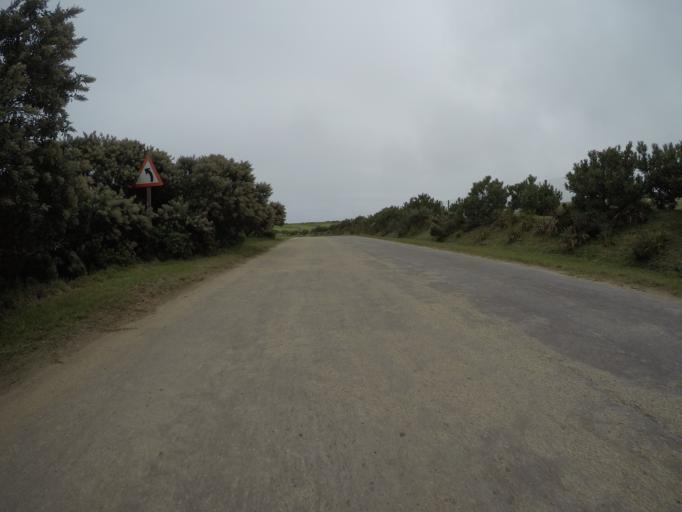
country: ZA
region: Eastern Cape
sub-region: Cacadu District Municipality
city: Kareedouw
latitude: -34.0709
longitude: 24.2339
